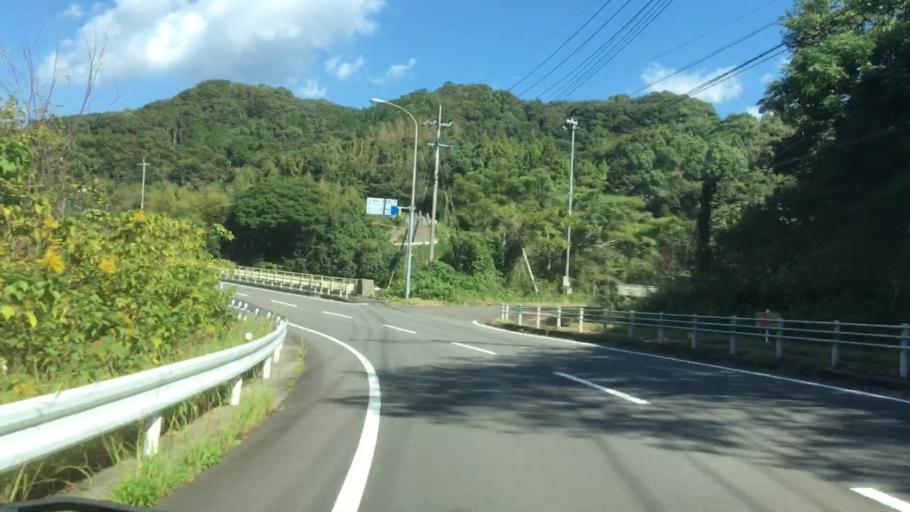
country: JP
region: Nagasaki
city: Sasebo
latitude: 33.0002
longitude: 129.6619
